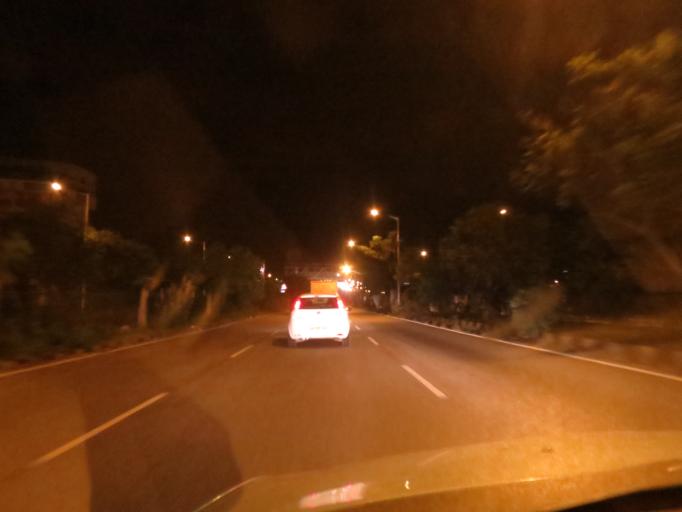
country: IN
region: Karnataka
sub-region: Bangalore Urban
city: Bangalore
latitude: 13.0219
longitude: 77.6486
